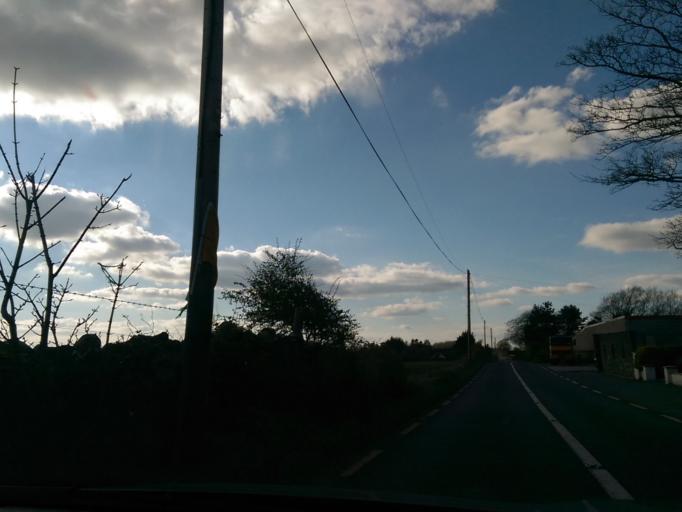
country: IE
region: Connaught
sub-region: County Galway
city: Loughrea
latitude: 53.2053
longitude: -8.4740
